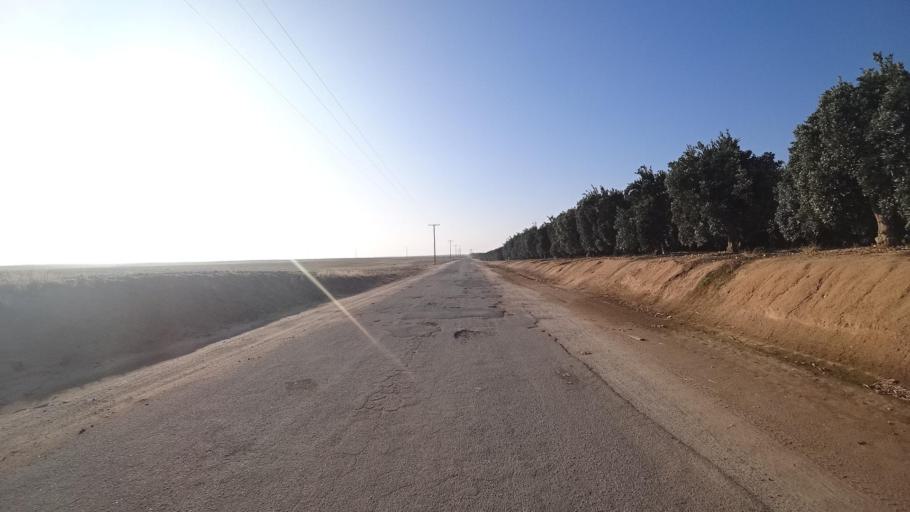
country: US
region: California
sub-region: Tulare County
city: Richgrove
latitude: 35.7664
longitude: -119.0807
